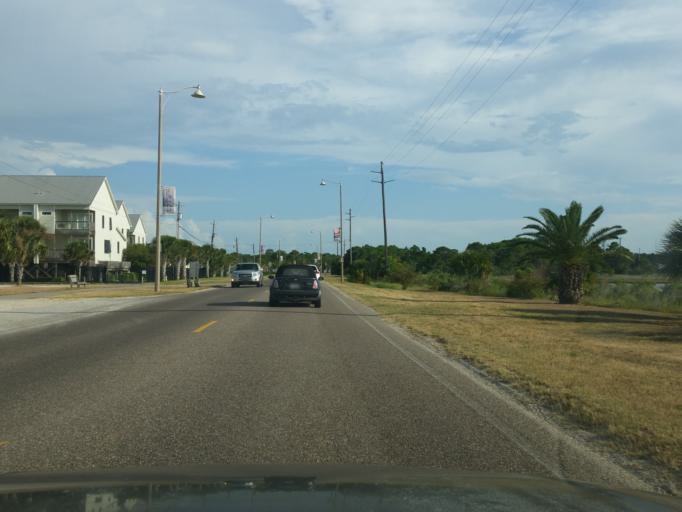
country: US
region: Alabama
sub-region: Mobile County
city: Dauphin Island
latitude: 30.2627
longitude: -88.1145
